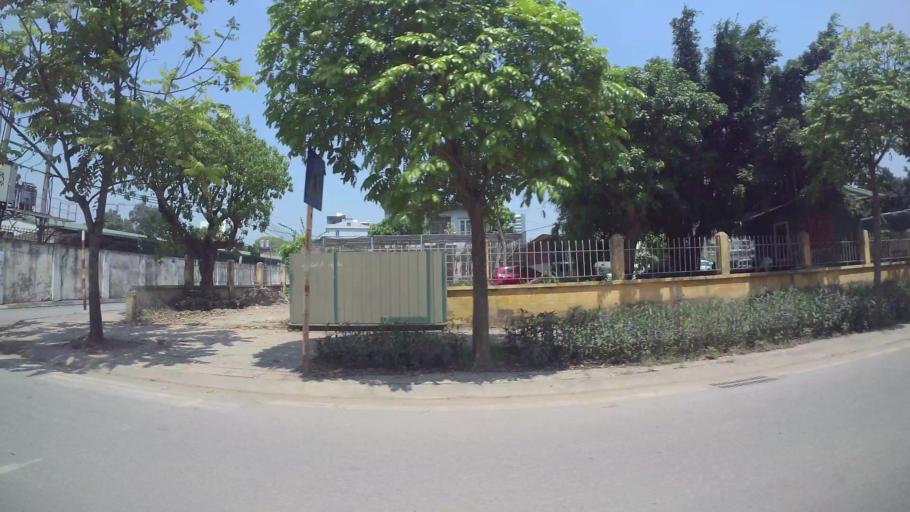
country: VN
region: Ha Noi
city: Hoan Kiem
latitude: 21.0452
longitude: 105.8843
